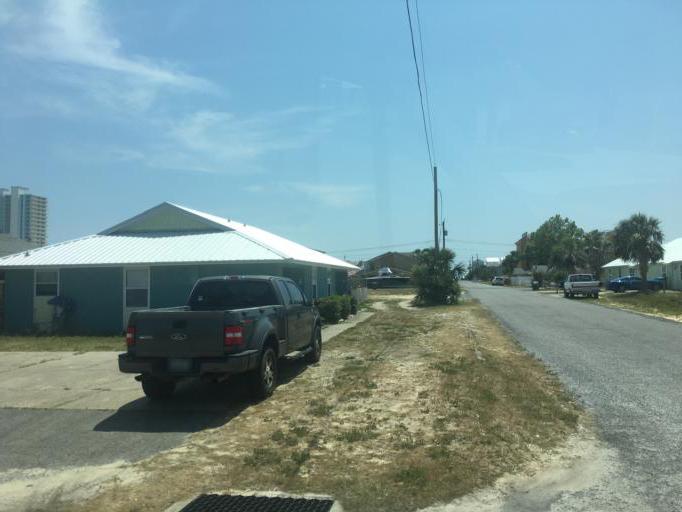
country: US
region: Florida
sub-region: Bay County
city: Lower Grand Lagoon
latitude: 30.1453
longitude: -85.7539
